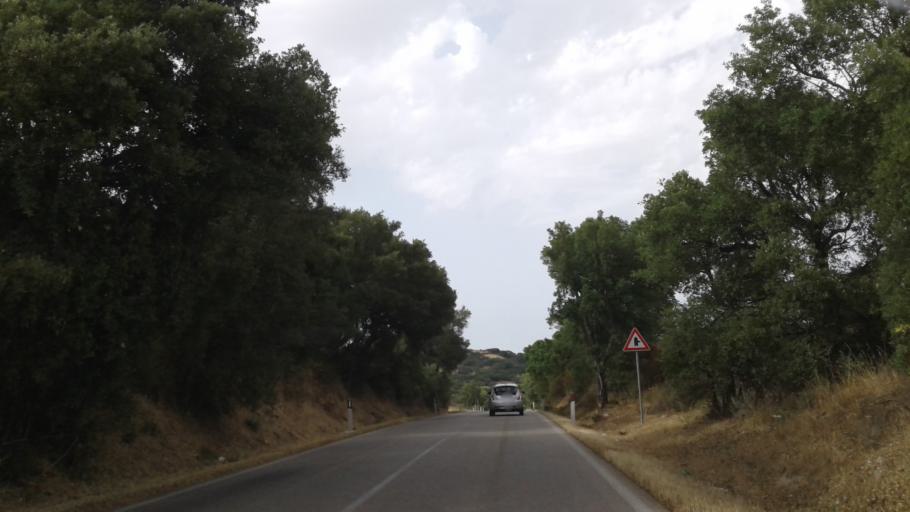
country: IT
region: Sardinia
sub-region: Provincia di Olbia-Tempio
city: Sant'Antonio di Gallura
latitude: 40.9553
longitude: 9.2944
